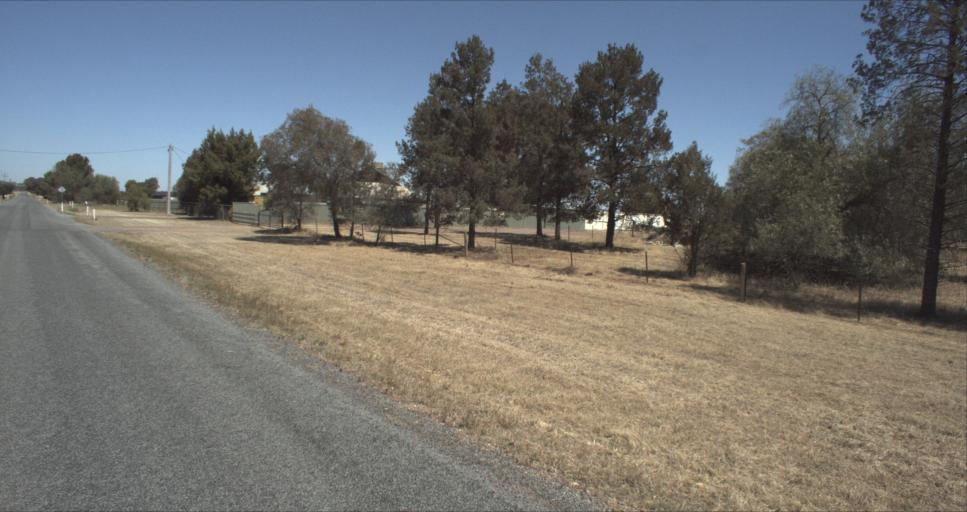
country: AU
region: New South Wales
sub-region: Leeton
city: Leeton
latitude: -34.5250
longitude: 146.4436
